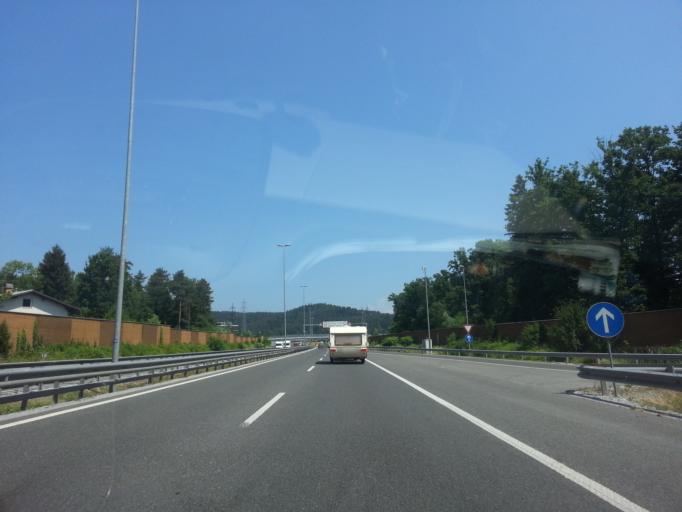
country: SI
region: Ljubljana
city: Ljubljana
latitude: 46.0755
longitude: 14.4600
